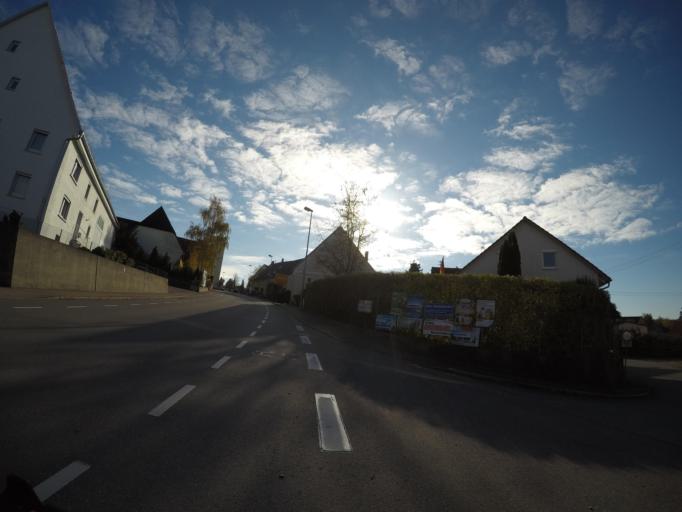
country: DE
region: Baden-Wuerttemberg
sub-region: Tuebingen Region
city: Herbertingen
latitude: 48.0616
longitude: 9.4360
